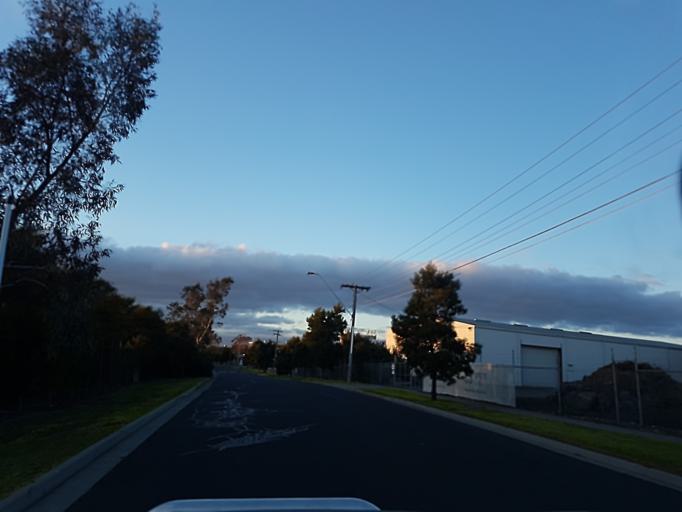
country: AU
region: Victoria
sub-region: Hume
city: Broadmeadows
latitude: -37.6806
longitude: 144.9220
